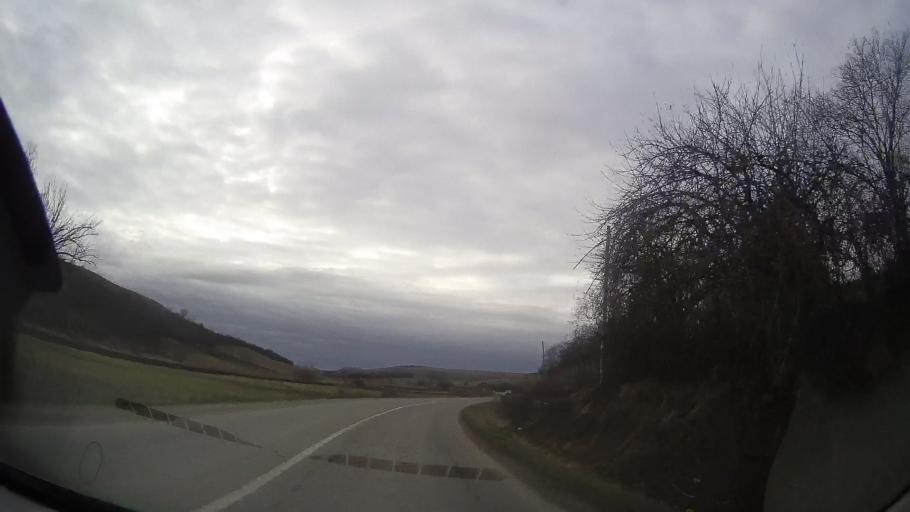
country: RO
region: Bistrita-Nasaud
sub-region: Comuna Budesti
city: Budesti
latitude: 46.8654
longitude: 24.2463
